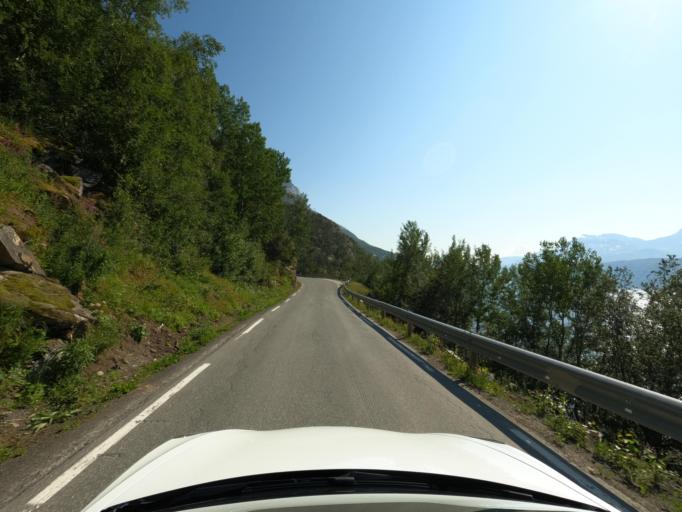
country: NO
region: Nordland
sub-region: Narvik
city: Narvik
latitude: 68.3666
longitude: 17.2563
